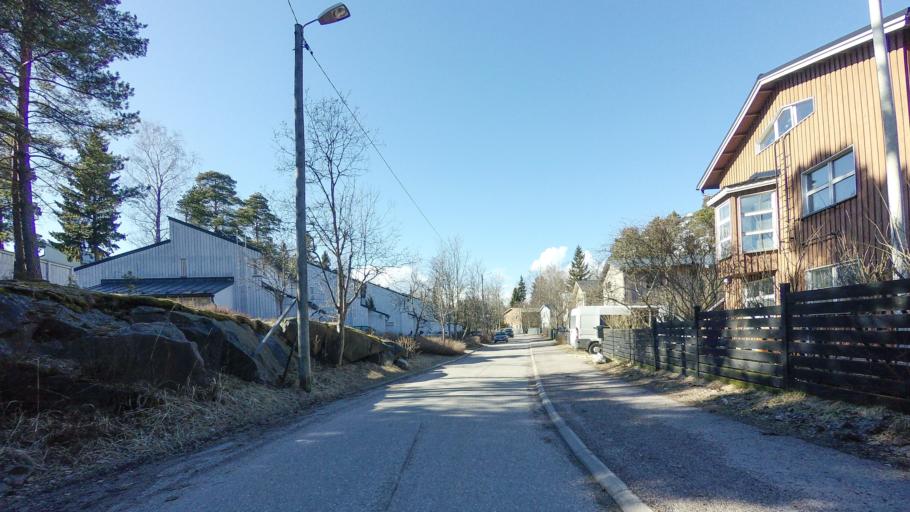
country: FI
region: Uusimaa
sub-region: Helsinki
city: Helsinki
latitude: 60.1609
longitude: 25.0680
